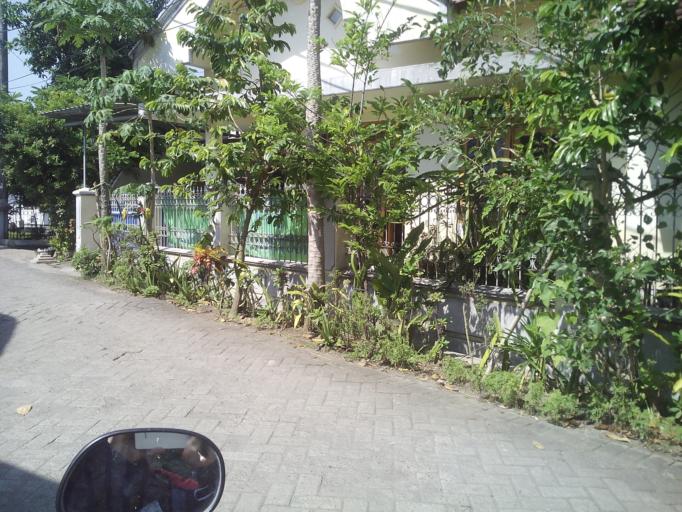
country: ID
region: East Java
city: Kloncing
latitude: -8.1806
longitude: 113.7235
